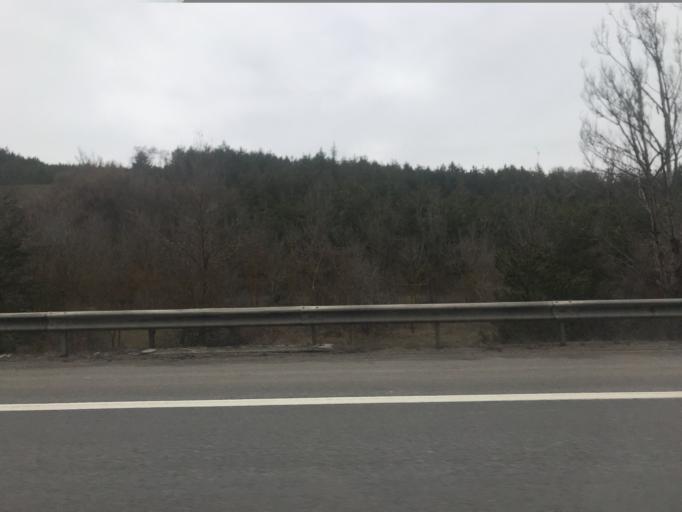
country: TR
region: Bolu
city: Bolu
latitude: 40.7394
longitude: 31.7922
